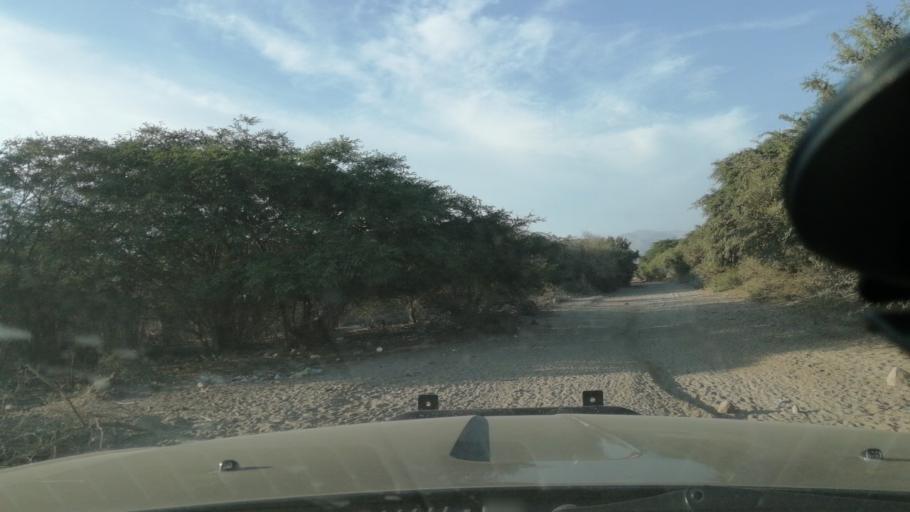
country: PE
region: Ica
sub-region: Provincia de Chincha
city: San Pedro
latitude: -13.3444
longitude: -76.1600
